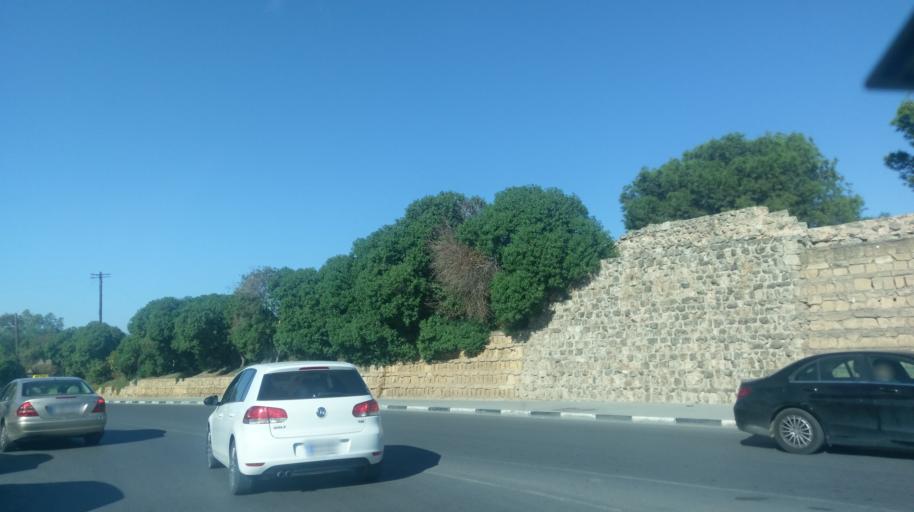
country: CY
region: Ammochostos
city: Famagusta
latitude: 35.1208
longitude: 33.9382
